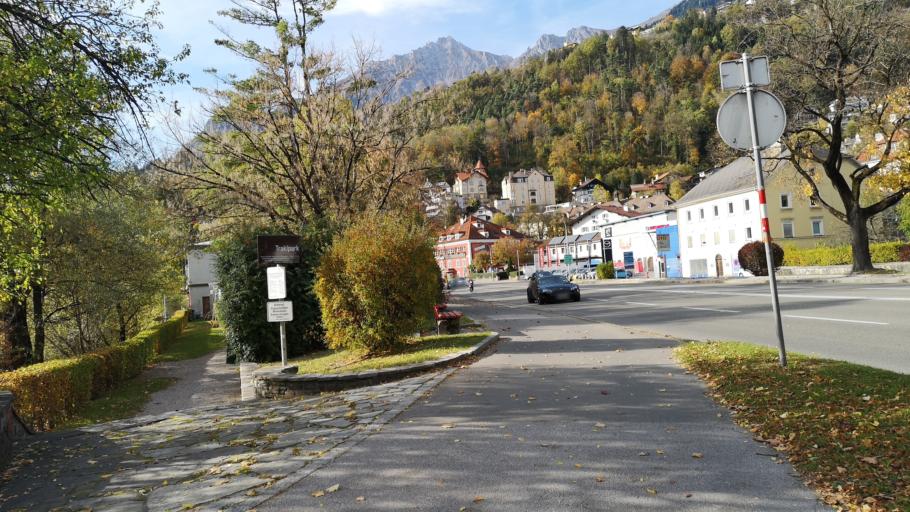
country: AT
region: Tyrol
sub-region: Innsbruck Stadt
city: Innsbruck
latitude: 47.2807
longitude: 11.4090
